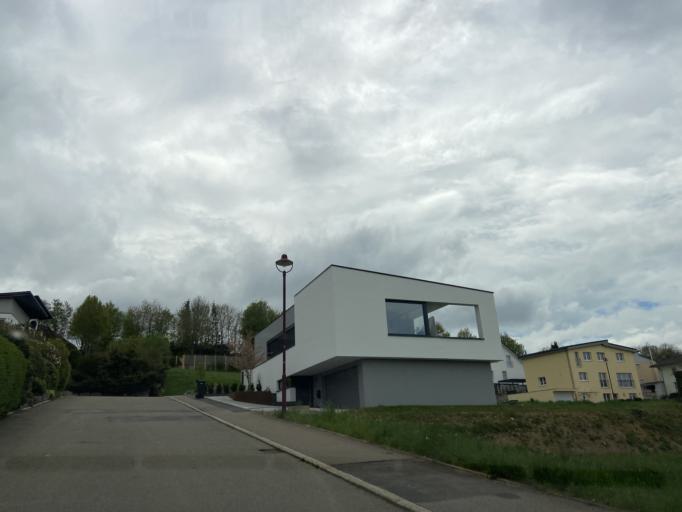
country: DE
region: Baden-Wuerttemberg
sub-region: Tuebingen Region
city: Sigmaringen
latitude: 48.0932
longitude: 9.2360
